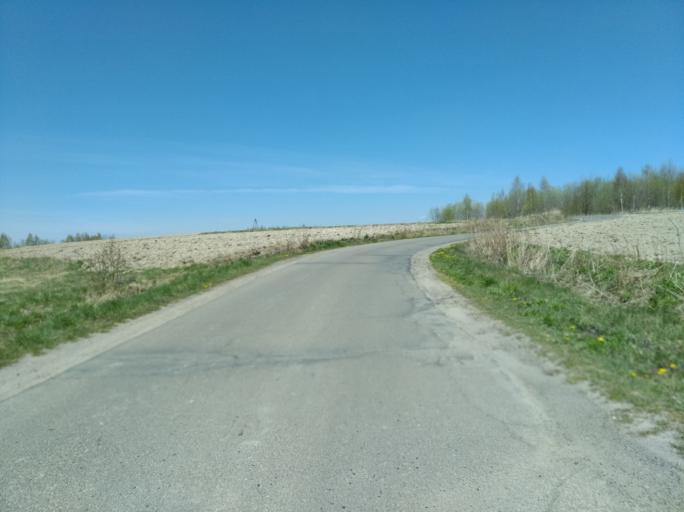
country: PL
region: Subcarpathian Voivodeship
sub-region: Powiat brzozowski
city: Jablonka
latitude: 49.7332
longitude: 22.1171
